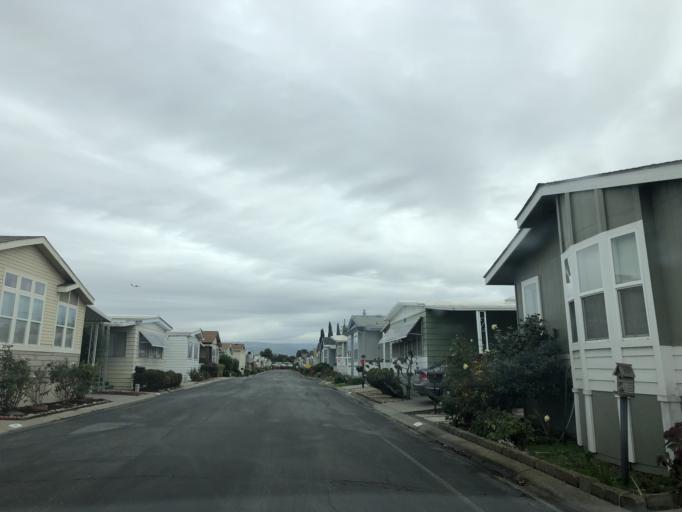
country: US
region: California
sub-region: Santa Clara County
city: Sunnyvale
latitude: 37.3998
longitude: -122.0021
